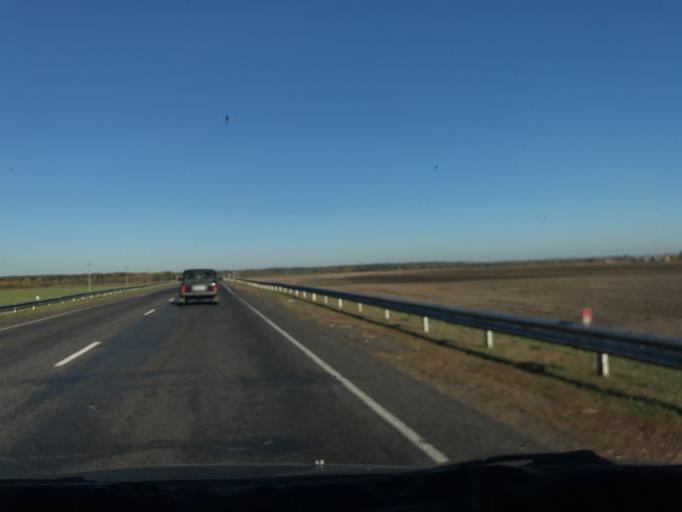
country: BY
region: Gomel
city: Kalinkavichy
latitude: 52.0360
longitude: 29.3443
